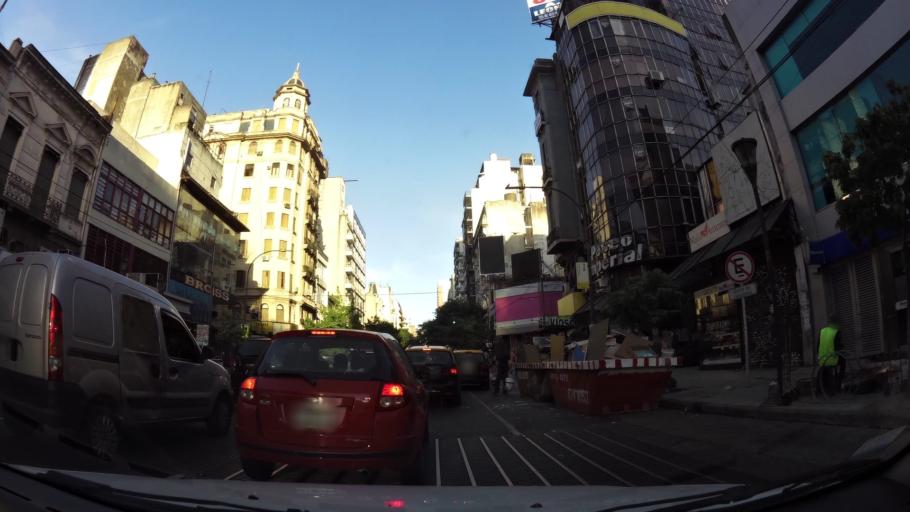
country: AR
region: Buenos Aires F.D.
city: Buenos Aires
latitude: -34.6048
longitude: -58.4026
